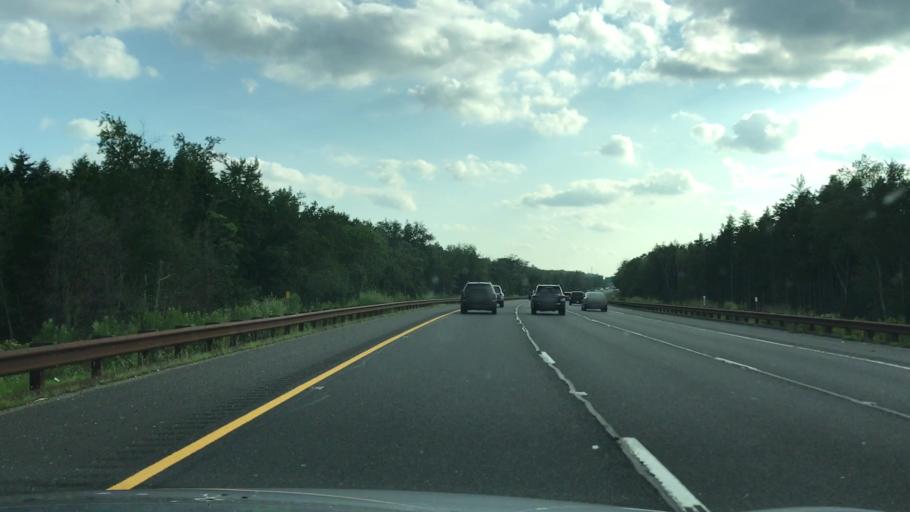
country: US
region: New Jersey
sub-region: Ocean County
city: Tuckerton
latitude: 39.6659
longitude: -74.3194
